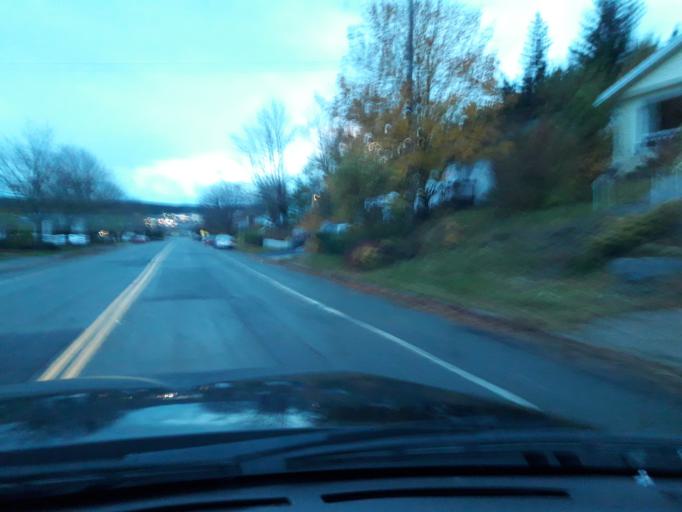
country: CA
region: Newfoundland and Labrador
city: St. John's
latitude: 47.5673
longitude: -52.7513
